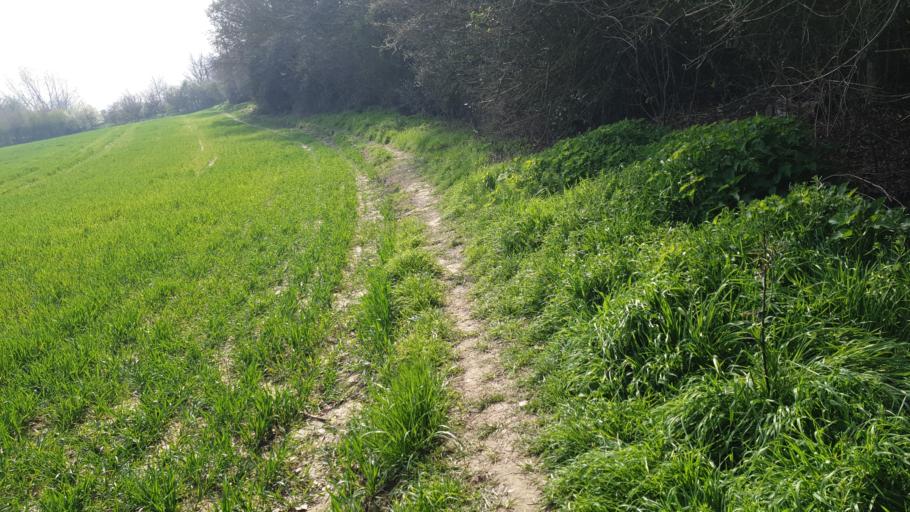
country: GB
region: England
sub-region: Essex
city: Mistley
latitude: 51.9192
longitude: 1.1454
